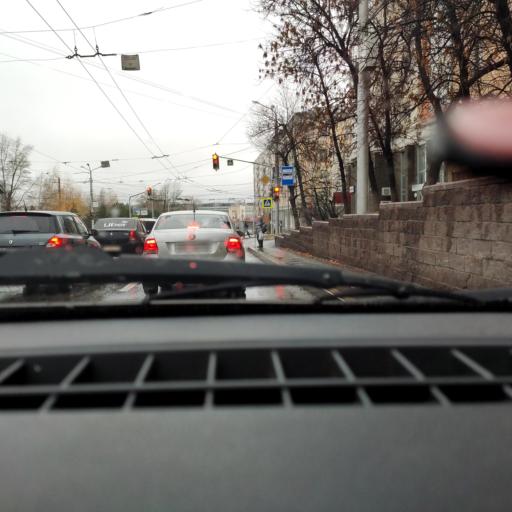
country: RU
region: Bashkortostan
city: Ufa
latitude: 54.7367
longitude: 55.9471
